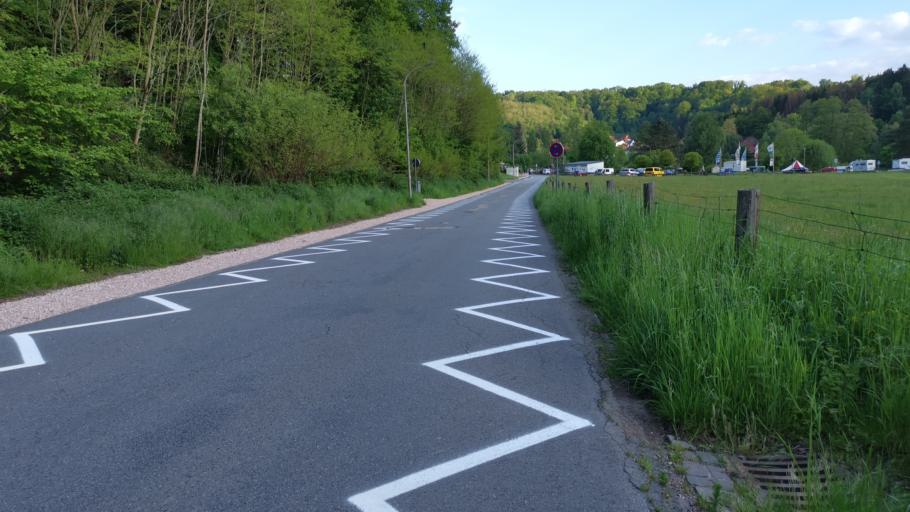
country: DE
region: Saarland
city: Kirkel
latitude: 49.2485
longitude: 7.1917
